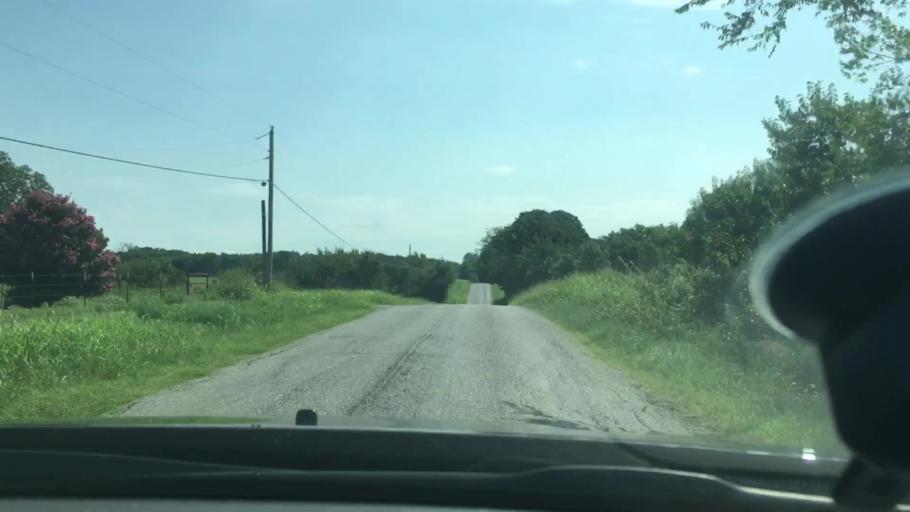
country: US
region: Oklahoma
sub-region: Bryan County
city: Colbert
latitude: 33.9110
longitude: -96.5239
